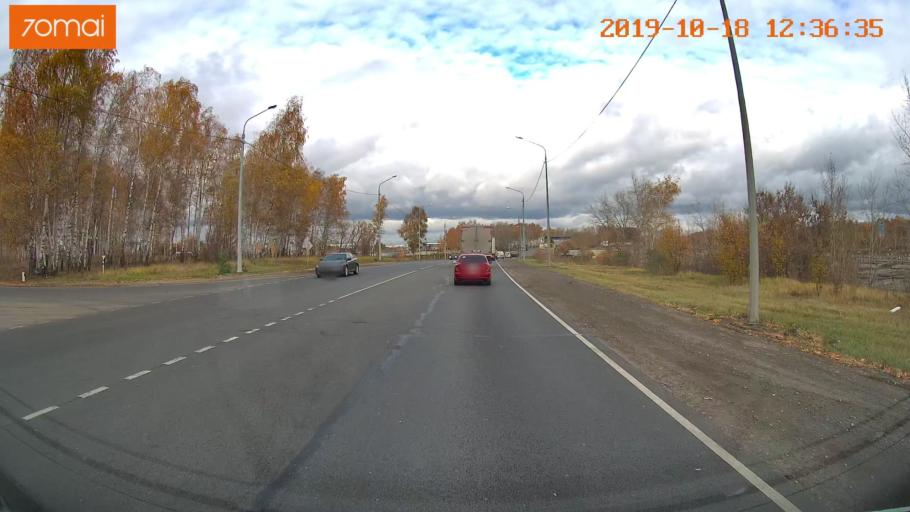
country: RU
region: Rjazan
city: Ryazan'
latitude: 54.6366
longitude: 39.6343
